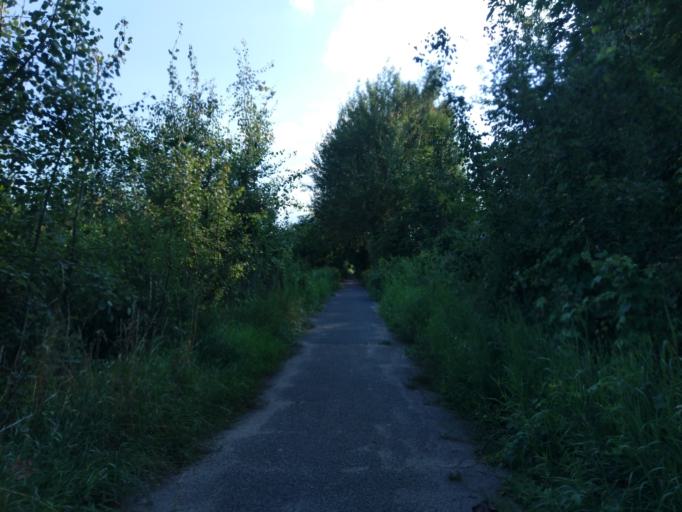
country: DE
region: Berlin
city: Lichterfelde
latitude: 52.4122
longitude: 13.2882
